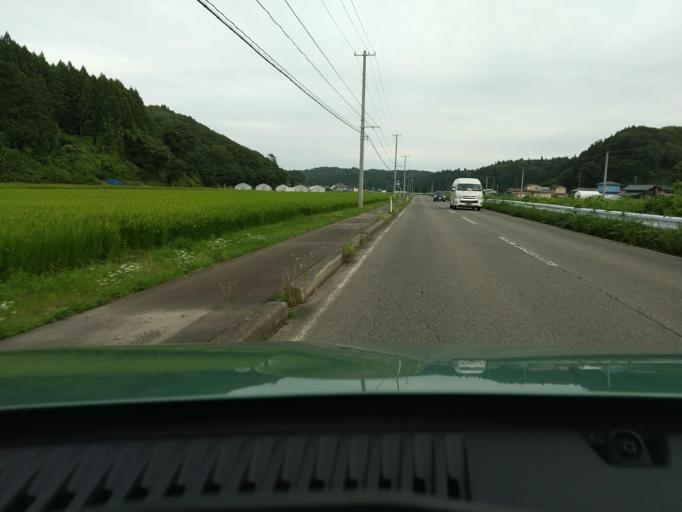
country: JP
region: Akita
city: Akita
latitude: 39.7860
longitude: 140.1230
